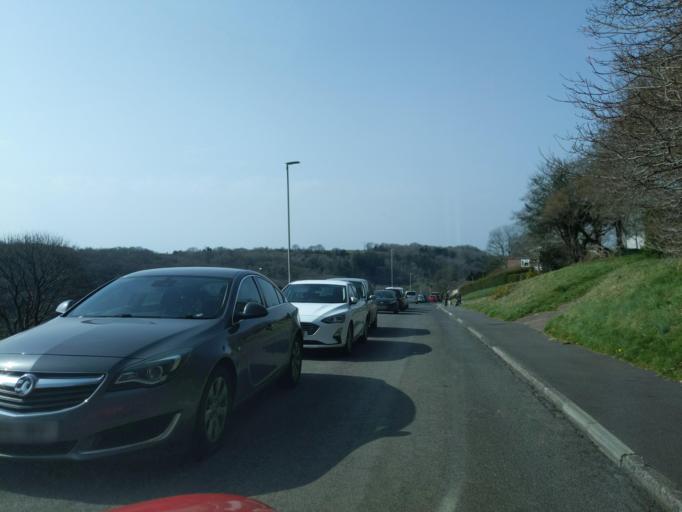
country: GB
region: England
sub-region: Plymouth
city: Plymouth
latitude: 50.4251
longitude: -4.1383
